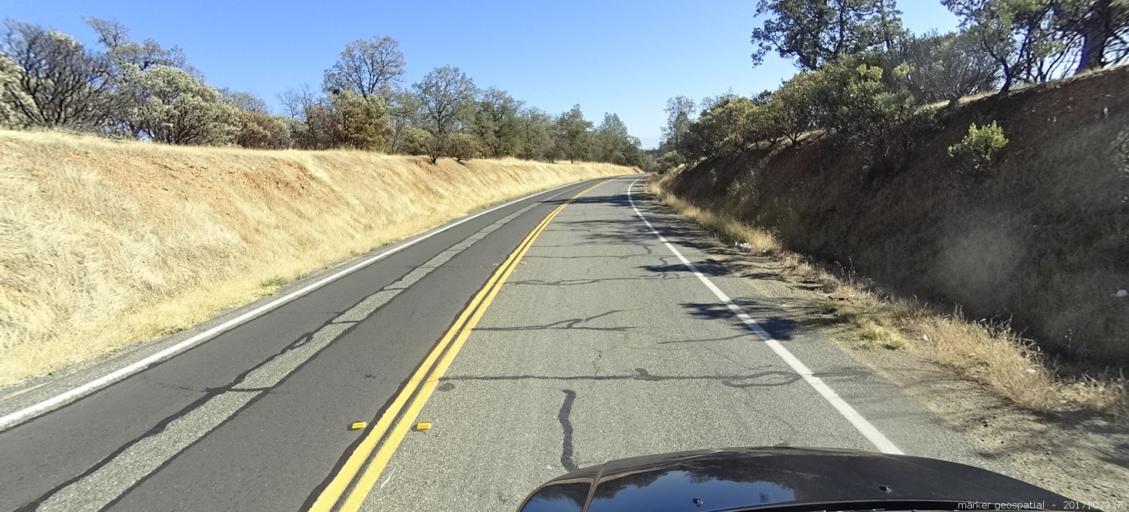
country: US
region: California
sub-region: Shasta County
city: Shasta
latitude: 40.4904
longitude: -122.5367
